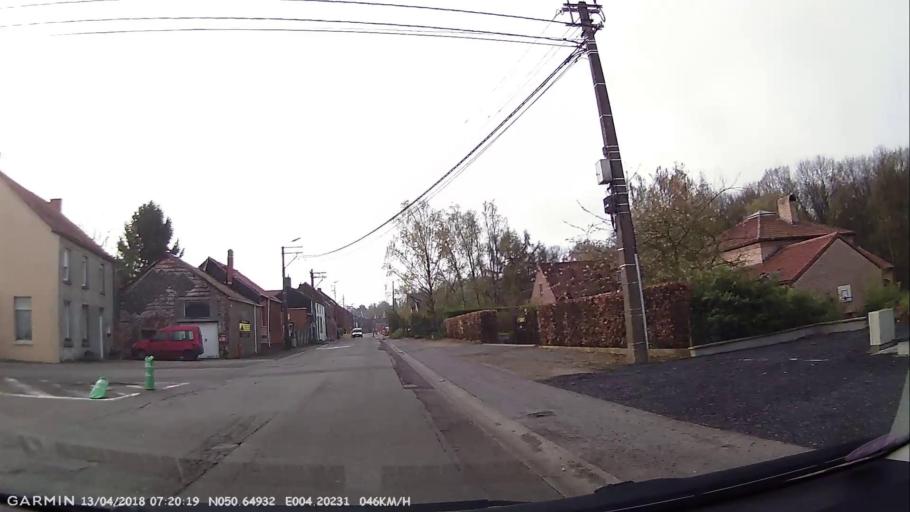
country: BE
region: Wallonia
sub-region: Province du Brabant Wallon
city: Tubize
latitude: 50.6493
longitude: 4.2024
